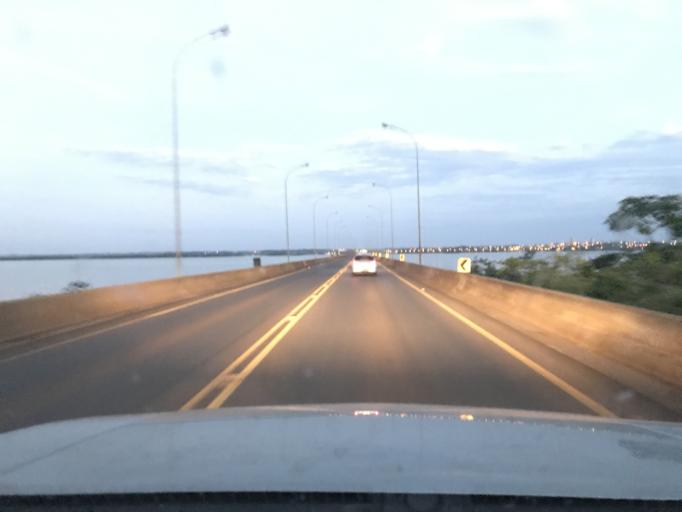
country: PY
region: Canindeyu
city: Salto del Guaira
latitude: -24.0448
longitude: -54.2719
